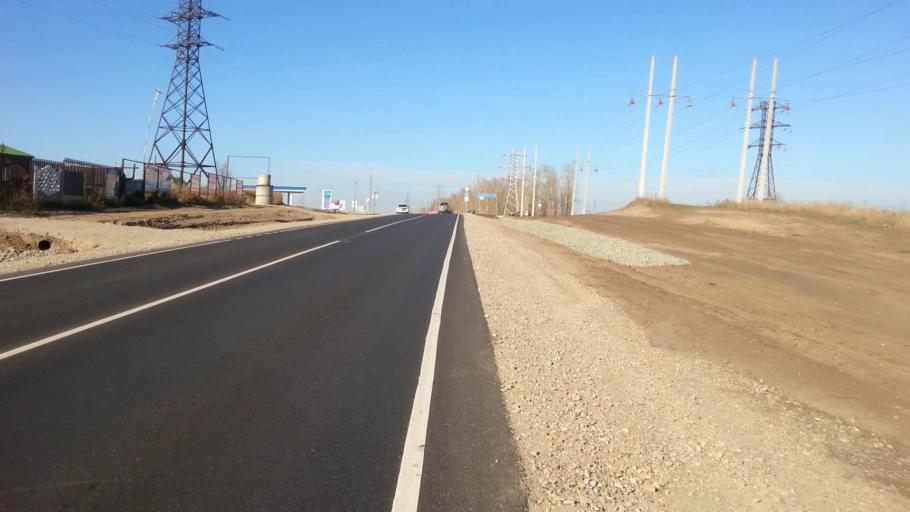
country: RU
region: Altai Krai
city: Sannikovo
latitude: 53.3353
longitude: 83.9384
